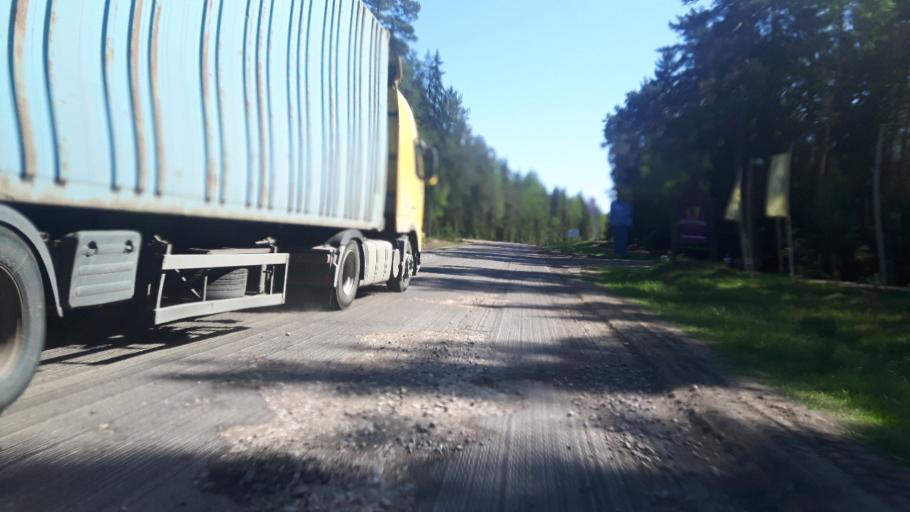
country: RU
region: Leningrad
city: Sosnovyy Bor
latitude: 60.2325
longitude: 29.0013
